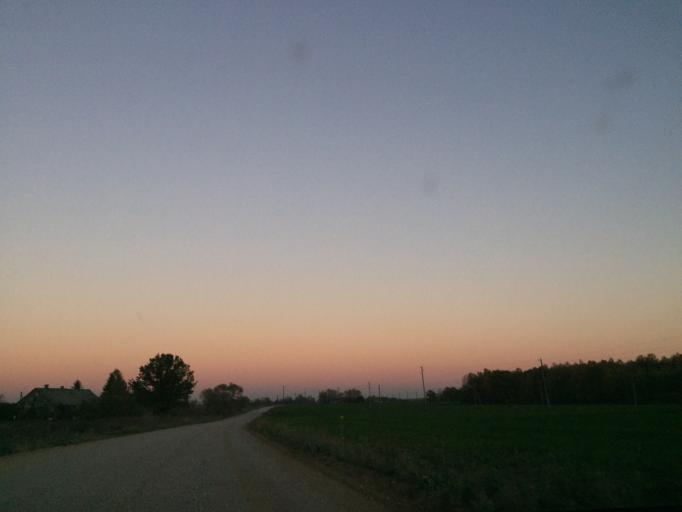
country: LT
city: Akmene
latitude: 56.3776
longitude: 22.7036
